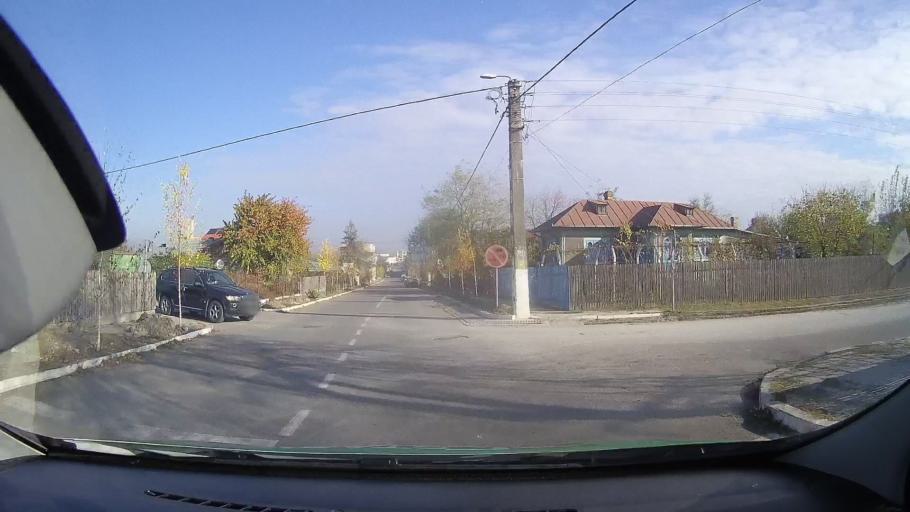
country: RO
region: Tulcea
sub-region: Comuna Mahmudia
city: Mahmudia
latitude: 45.0862
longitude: 29.0855
